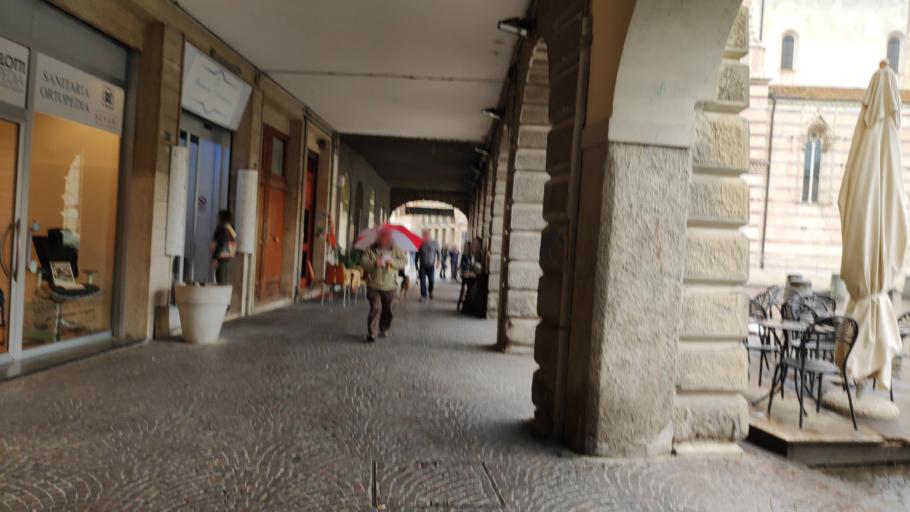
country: IT
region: Tuscany
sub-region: Provincia di Grosseto
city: Grosseto
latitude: 42.7595
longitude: 11.1135
